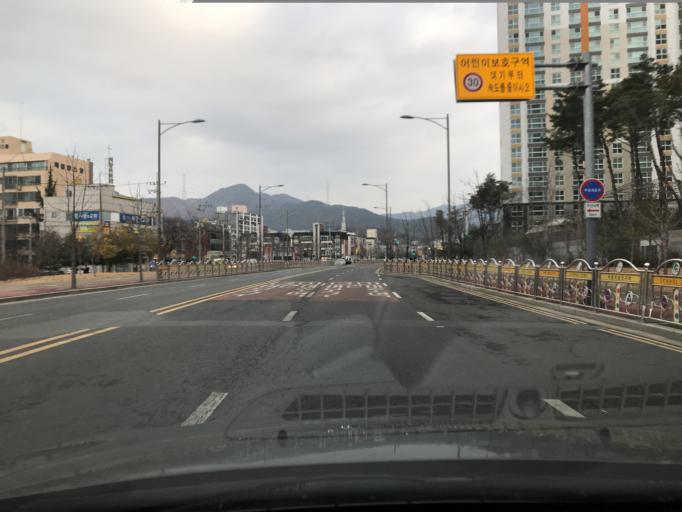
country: KR
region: Daegu
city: Hwawon
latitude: 35.6936
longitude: 128.4501
